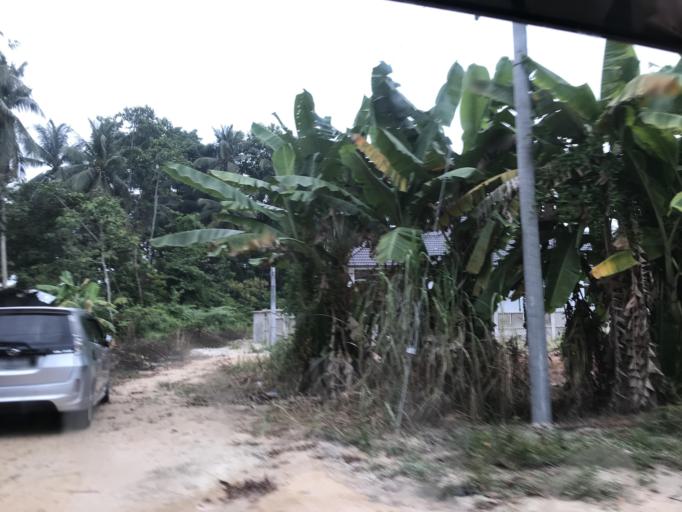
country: MY
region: Kelantan
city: Tumpat
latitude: 6.1672
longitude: 102.2054
